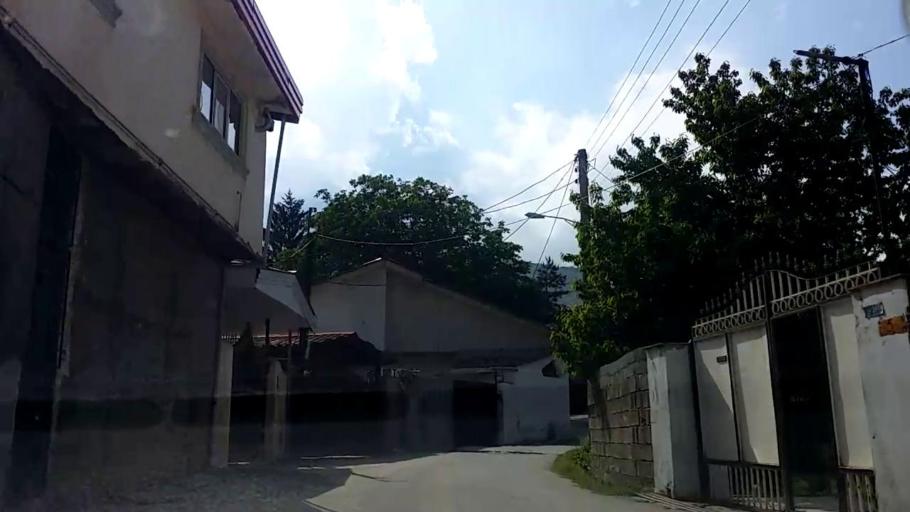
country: IR
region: Mazandaran
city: `Abbasabad
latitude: 36.5078
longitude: 51.1652
